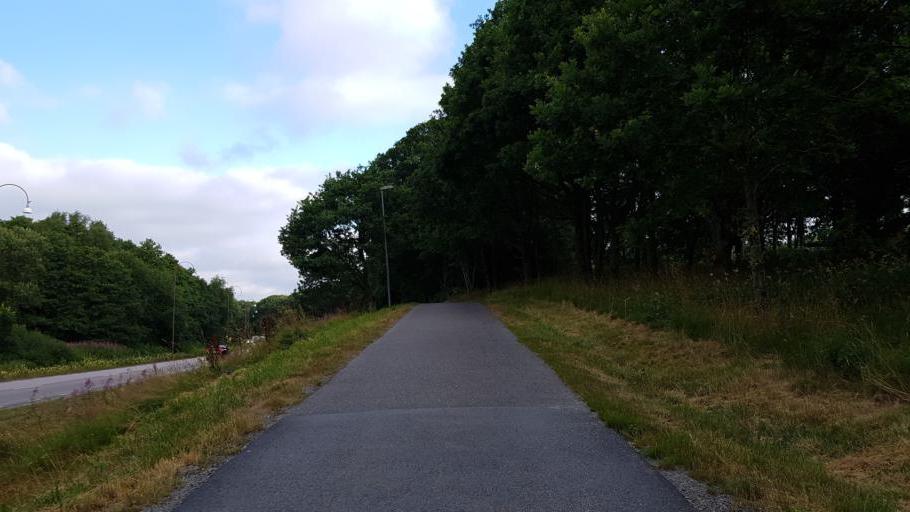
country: SE
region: Vaestra Goetaland
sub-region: Harryda Kommun
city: Molnlycke
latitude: 57.6578
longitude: 12.1059
